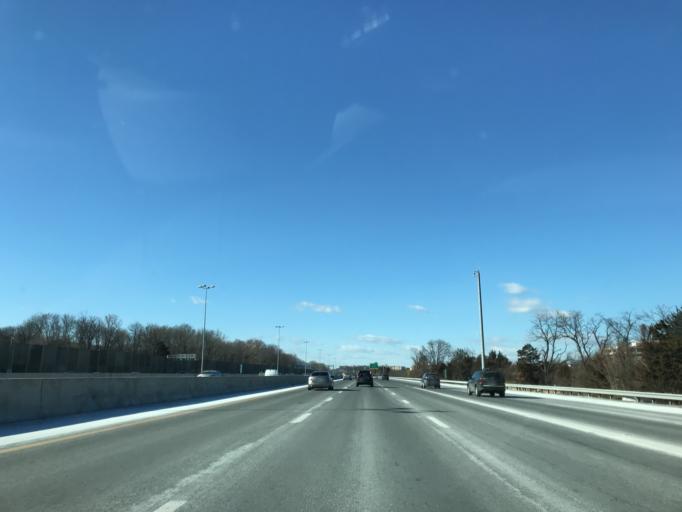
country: US
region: Virginia
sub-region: Fairfax County
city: Huntington
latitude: 38.8017
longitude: -77.0870
